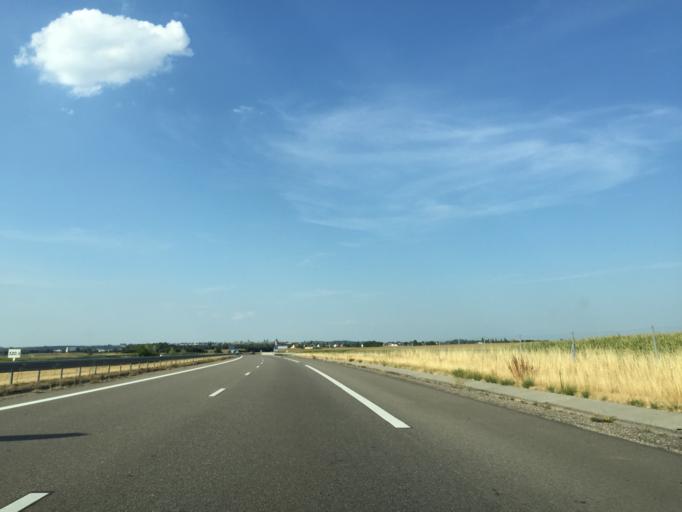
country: FR
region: Alsace
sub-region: Departement du Bas-Rhin
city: Innenheim
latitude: 48.5107
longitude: 7.5821
